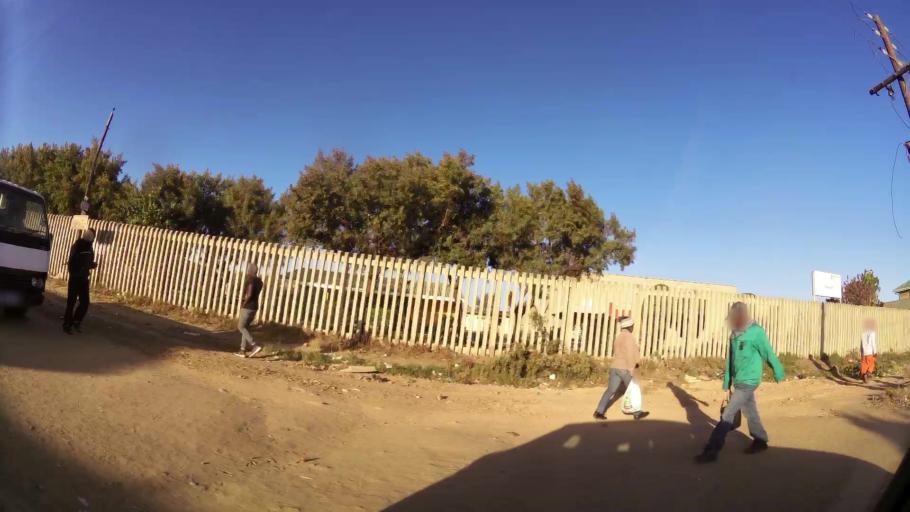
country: ZA
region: Gauteng
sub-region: City of Johannesburg Metropolitan Municipality
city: Diepsloot
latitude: -25.9372
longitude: 28.0144
